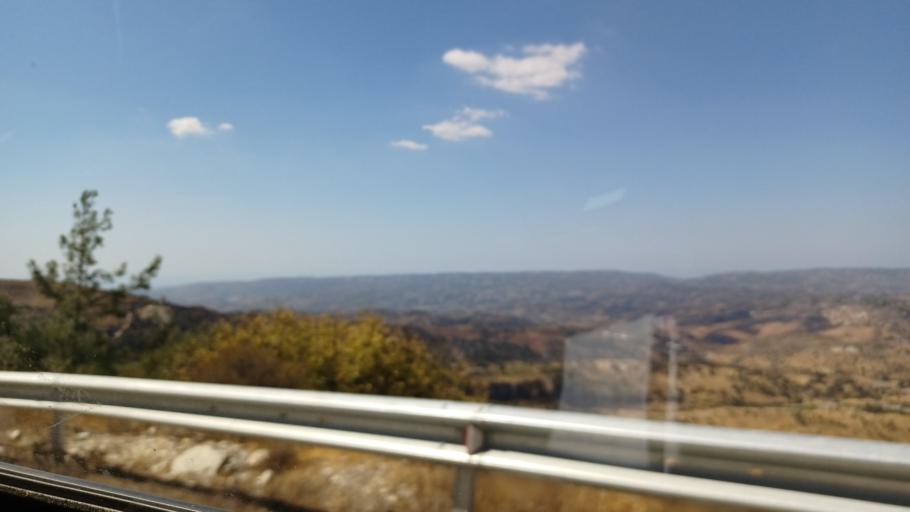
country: CY
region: Pafos
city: Mesogi
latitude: 34.9039
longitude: 32.6180
